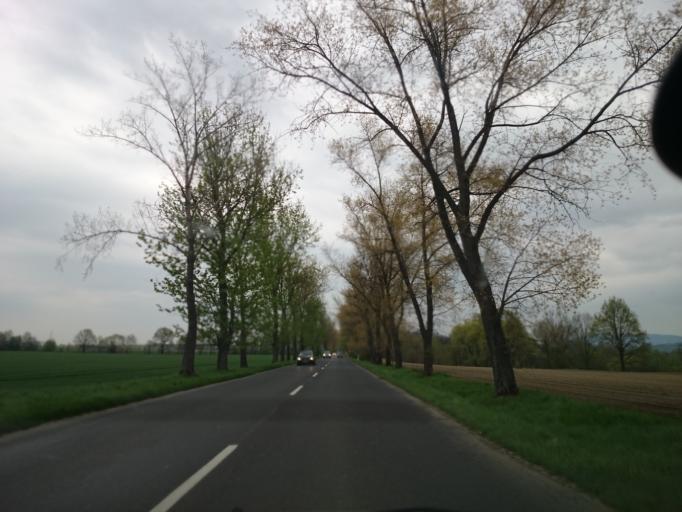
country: PL
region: Opole Voivodeship
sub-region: Powiat nyski
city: Glucholazy
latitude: 50.3591
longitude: 17.3770
